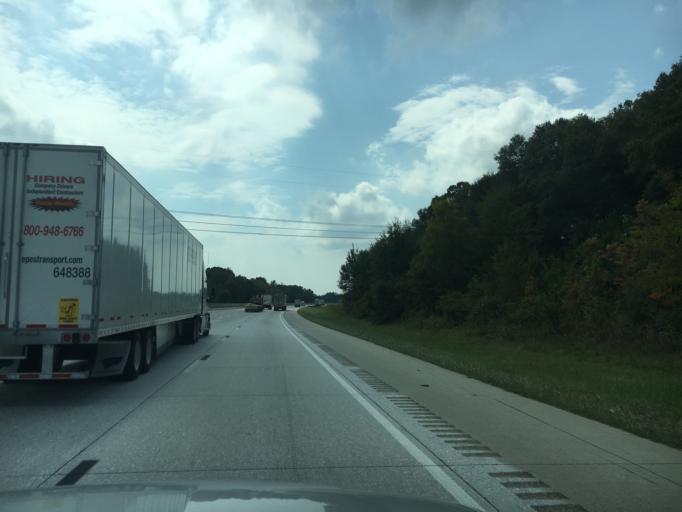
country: US
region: South Carolina
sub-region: Anderson County
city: Piedmont
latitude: 34.6870
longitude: -82.5130
